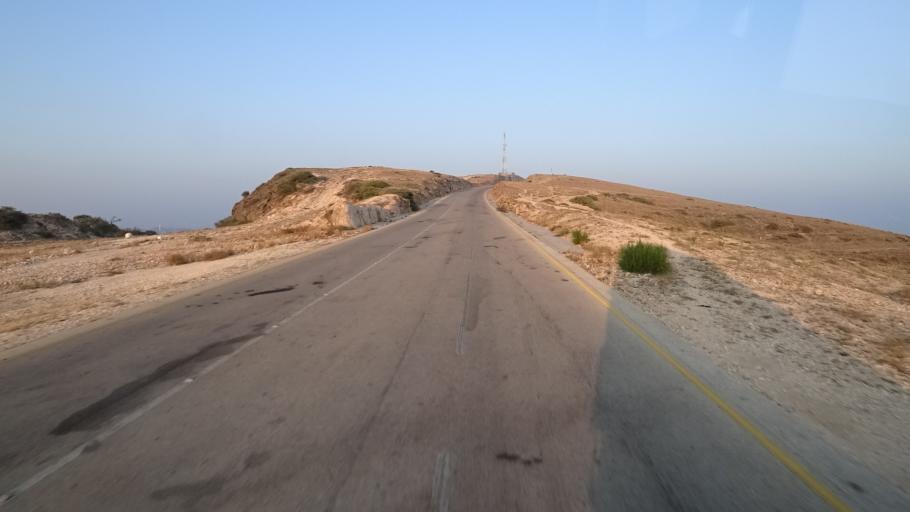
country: OM
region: Zufar
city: Salalah
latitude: 16.8219
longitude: 53.6424
